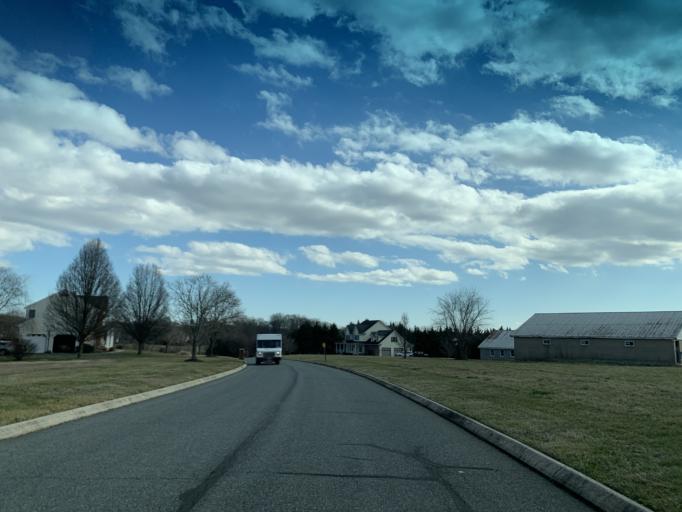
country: US
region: Maryland
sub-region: Harford County
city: Riverside
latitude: 39.5046
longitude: -76.2648
